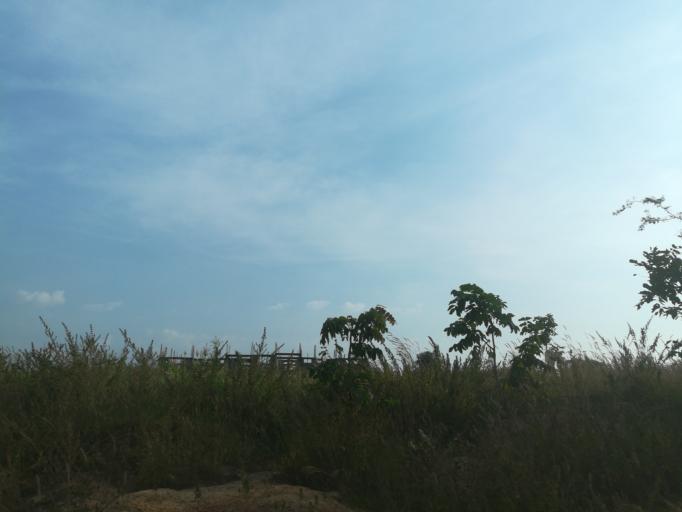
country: NG
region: Abuja Federal Capital Territory
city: Abuja
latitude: 9.0907
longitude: 7.3723
